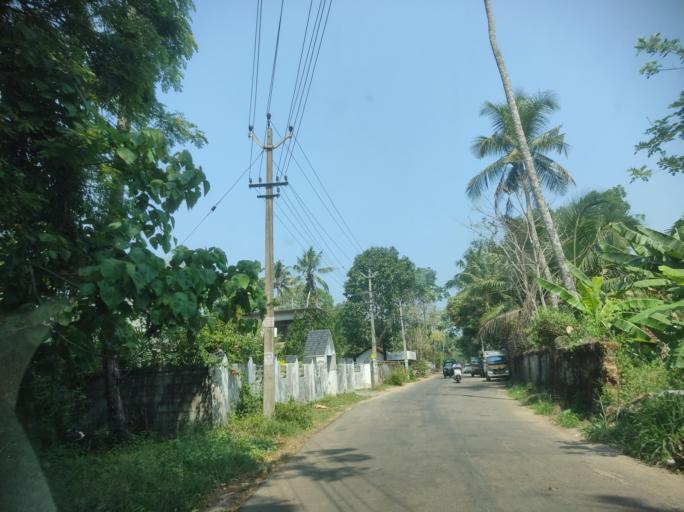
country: IN
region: Kerala
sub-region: Alappuzha
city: Vayalar
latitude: 9.6877
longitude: 76.3264
